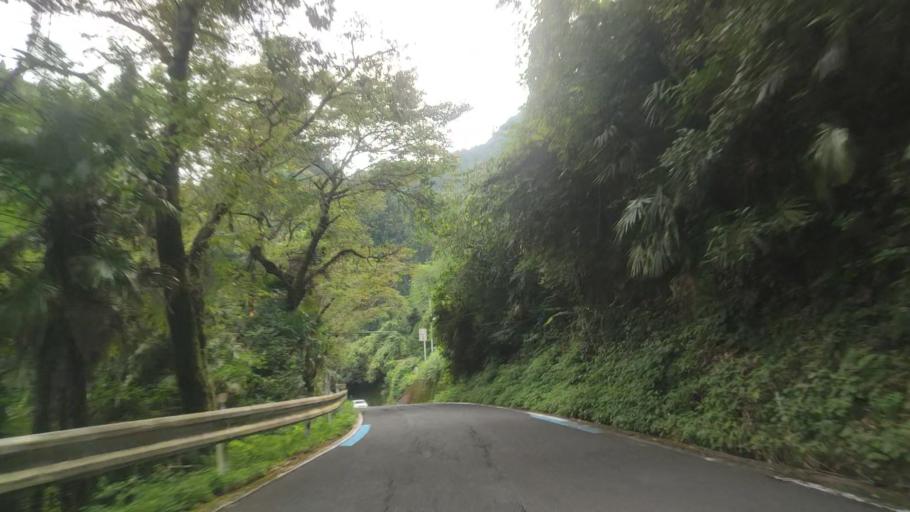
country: JP
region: Wakayama
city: Koya
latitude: 34.2462
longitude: 135.5461
